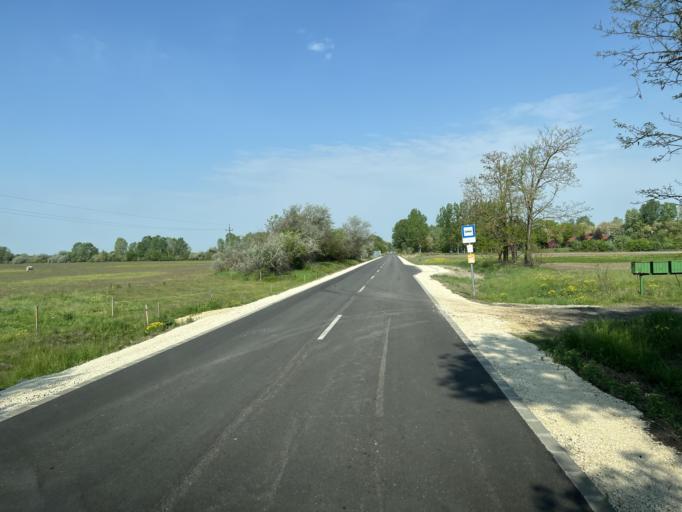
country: HU
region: Pest
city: Kocser
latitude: 46.9956
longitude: 19.9457
